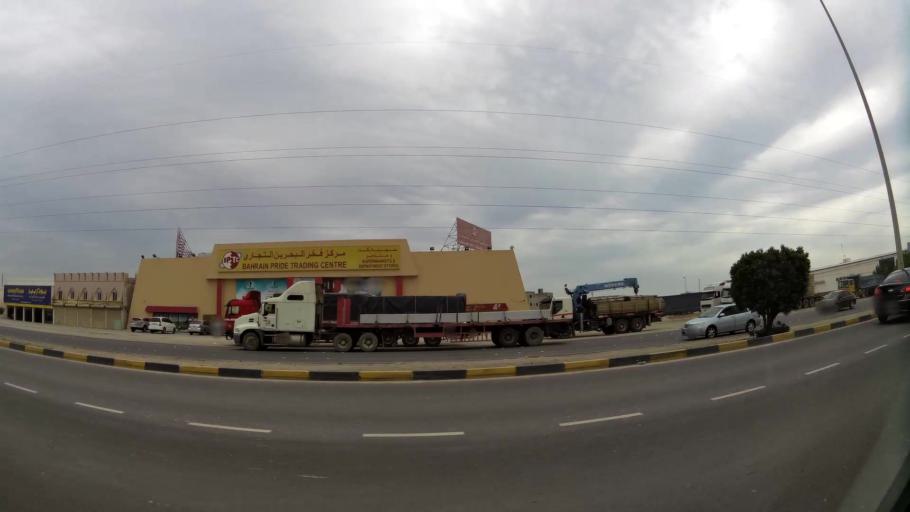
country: BH
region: Northern
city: Sitrah
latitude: 26.1553
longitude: 50.6111
